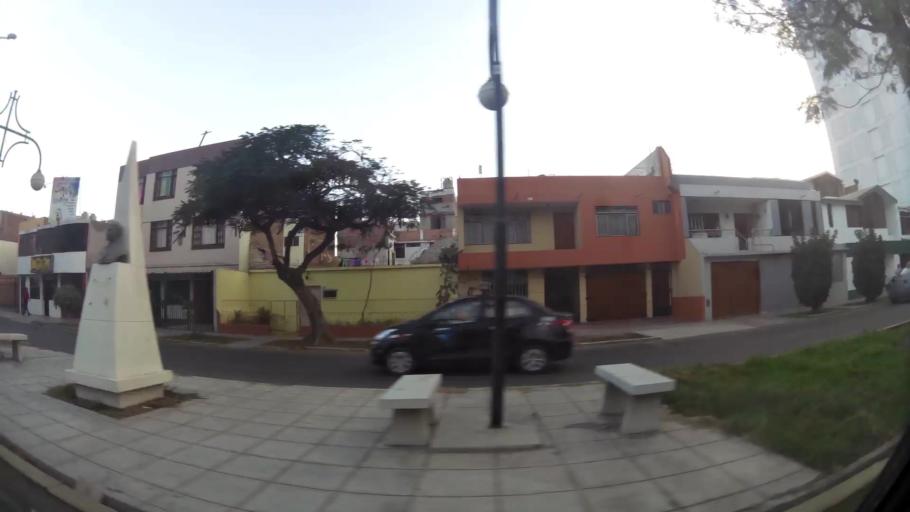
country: PE
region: La Libertad
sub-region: Provincia de Trujillo
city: Trujillo
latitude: -8.0997
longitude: -79.0332
